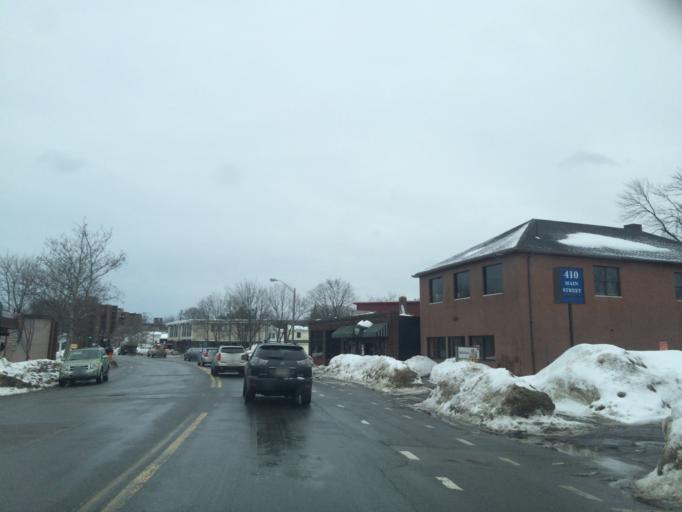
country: US
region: Massachusetts
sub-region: Middlesex County
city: Watertown
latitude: 42.3703
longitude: -71.1941
